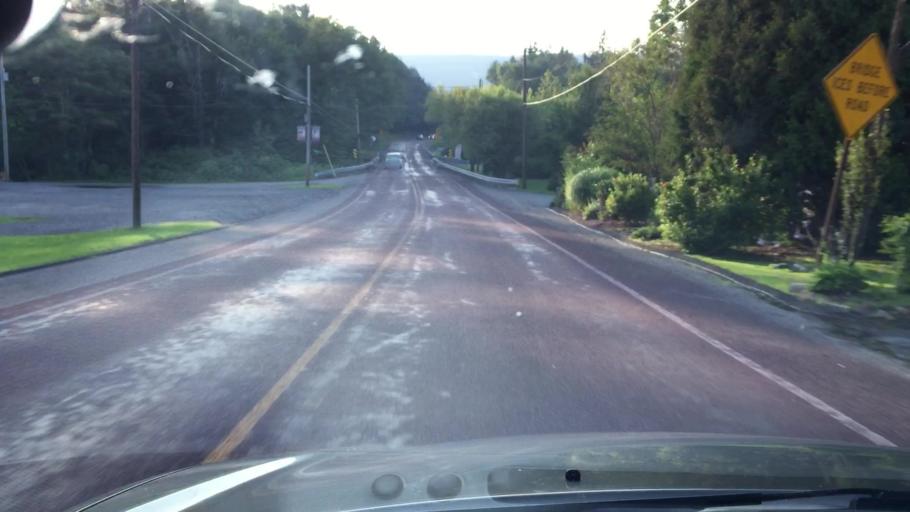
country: US
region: Pennsylvania
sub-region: Carbon County
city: Weatherly
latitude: 40.9161
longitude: -75.8541
